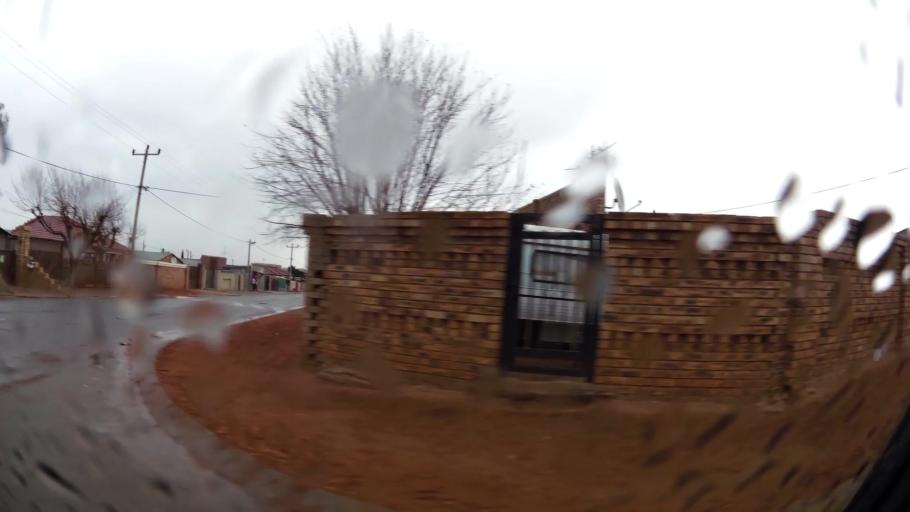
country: ZA
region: Gauteng
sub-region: West Rand District Municipality
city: Randfontein
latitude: -26.1768
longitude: 27.7834
